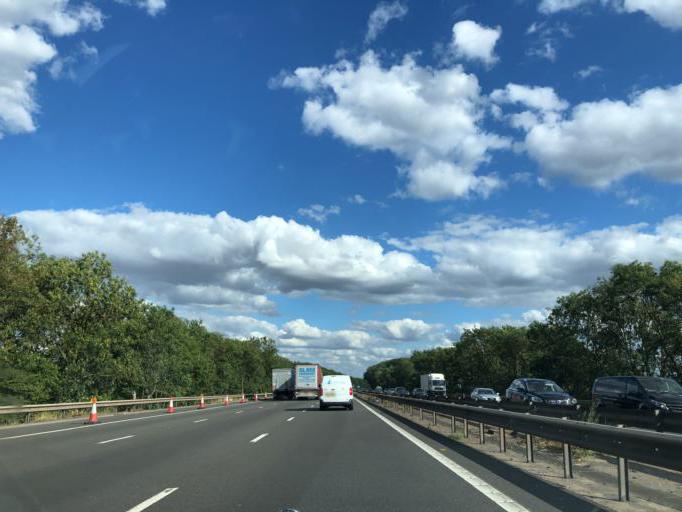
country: GB
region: England
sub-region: Milton Keynes
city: Gayhurst
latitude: 52.1046
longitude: -0.7759
